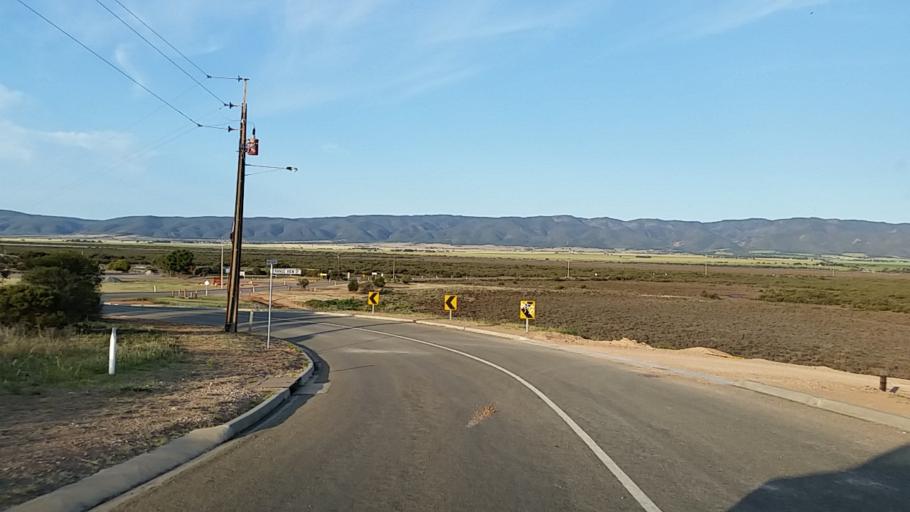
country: AU
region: South Australia
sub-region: Port Pirie City and Dists
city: Port Pirie
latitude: -33.1026
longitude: 138.0327
